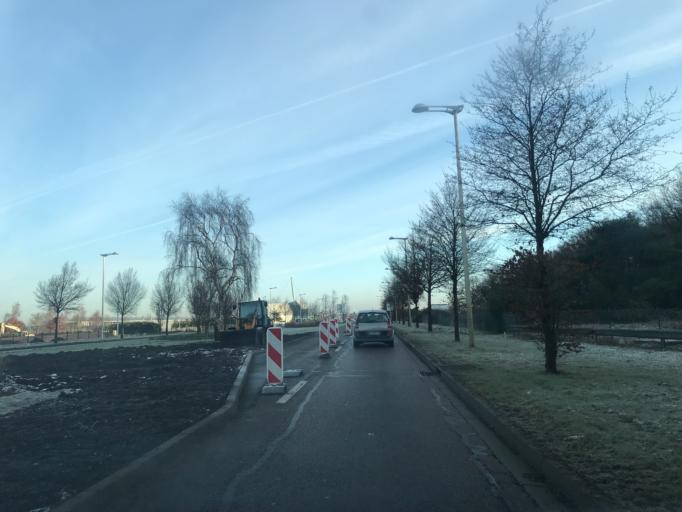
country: FR
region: Haute-Normandie
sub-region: Departement de la Seine-Maritime
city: Le Grand-Quevilly
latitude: 49.3899
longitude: 1.0570
